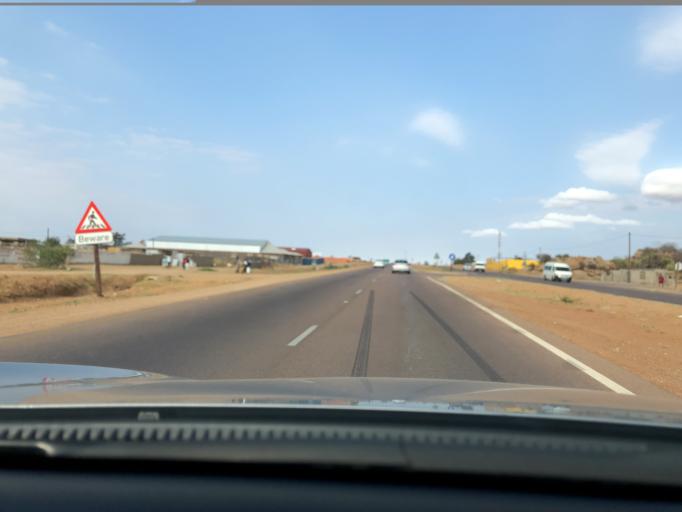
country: ZA
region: Limpopo
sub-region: Capricorn District Municipality
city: Mankoeng
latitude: -23.8906
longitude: 29.6615
